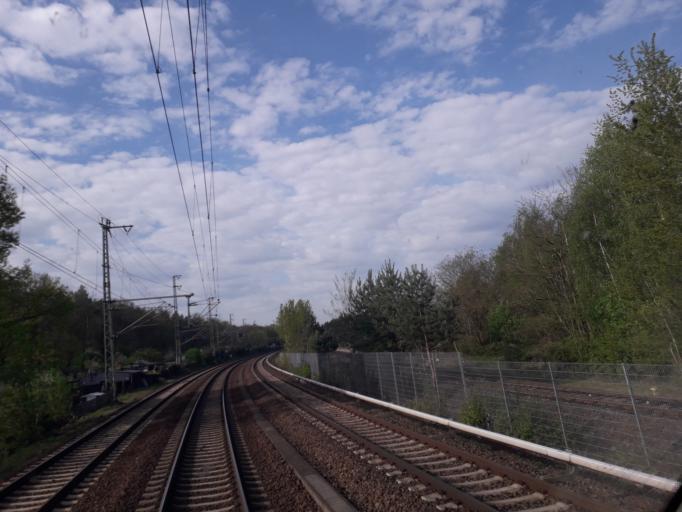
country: DE
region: Berlin
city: Grunewald
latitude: 52.4807
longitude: 13.2532
